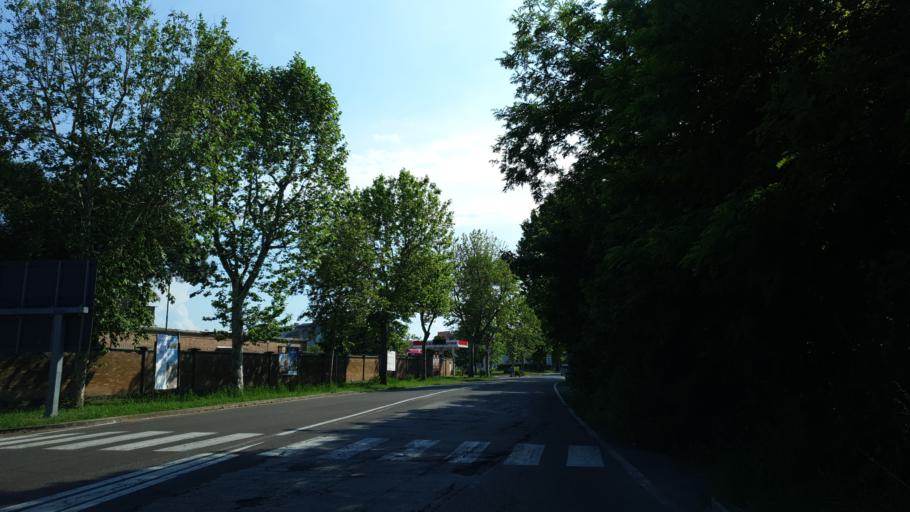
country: IT
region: Emilia-Romagna
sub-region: Provincia di Ravenna
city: Ravenna
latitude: 44.4267
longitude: 12.2148
